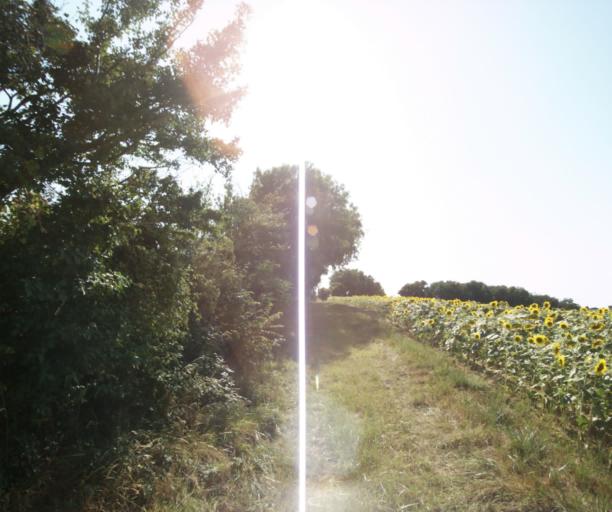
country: FR
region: Midi-Pyrenees
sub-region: Departement de la Haute-Garonne
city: Avignonet-Lauragais
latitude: 43.4254
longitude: 1.8061
